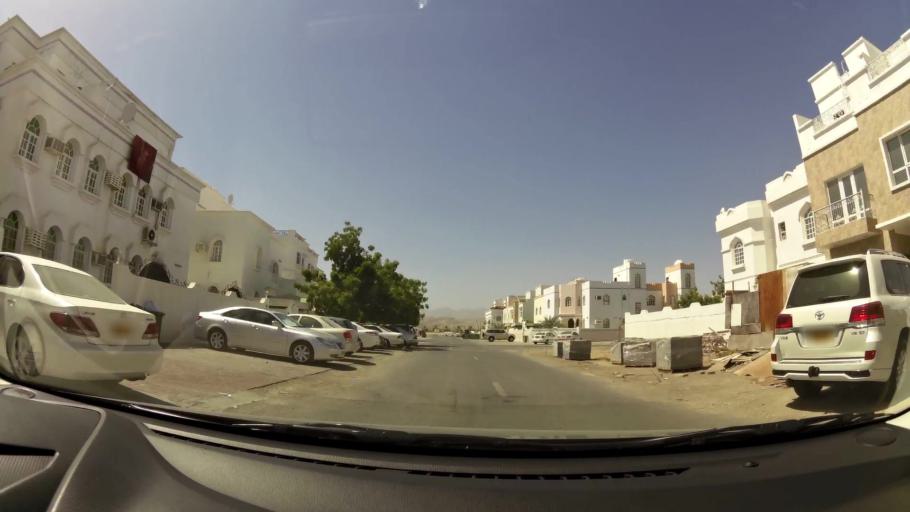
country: OM
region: Muhafazat Masqat
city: As Sib al Jadidah
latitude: 23.5925
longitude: 58.2440
